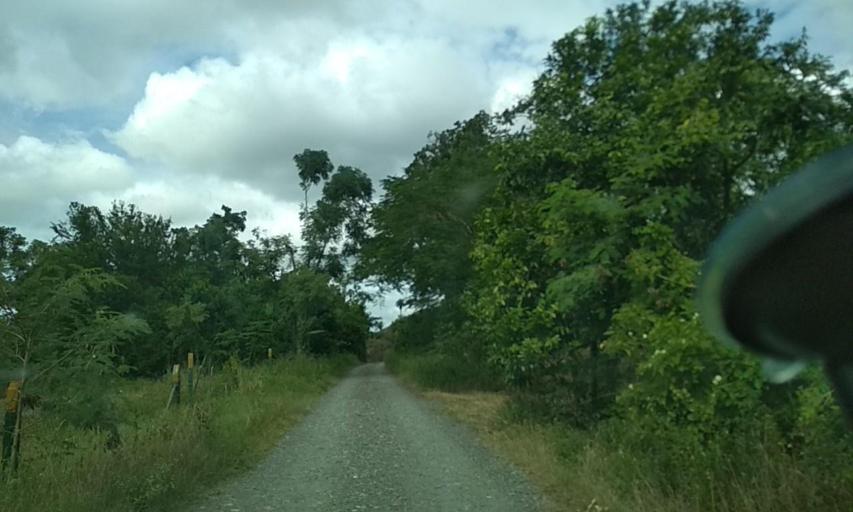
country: MX
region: Veracruz
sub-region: Papantla
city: Residencial Tajin
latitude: 20.6349
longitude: -97.3810
